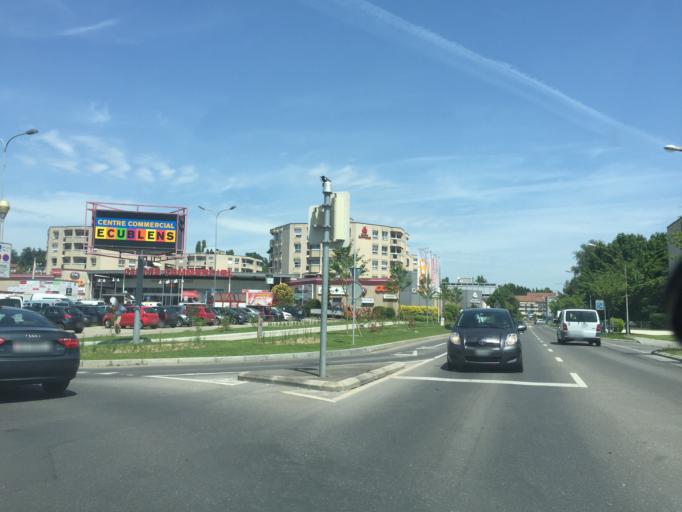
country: CH
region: Vaud
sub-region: Ouest Lausannois District
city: Chavannes
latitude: 46.5329
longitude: 6.5666
